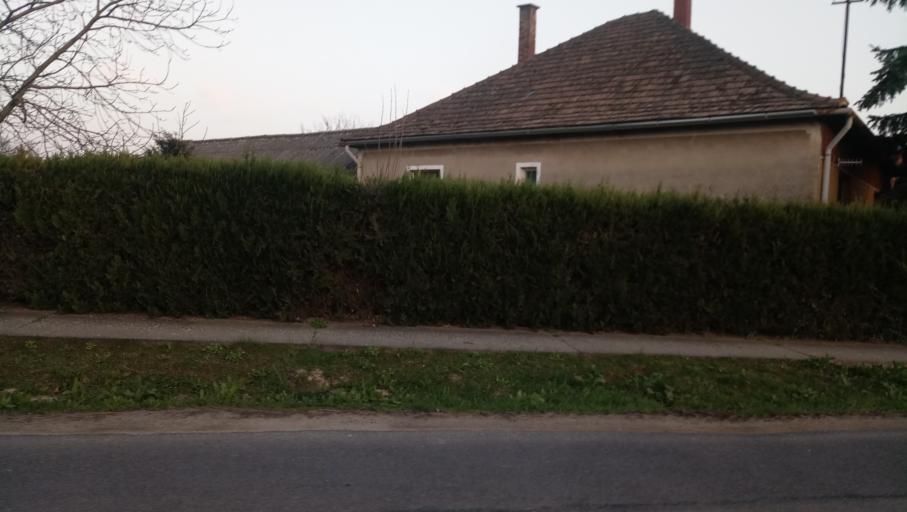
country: HU
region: Somogy
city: Nagybajom
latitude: 46.4200
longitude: 17.5980
